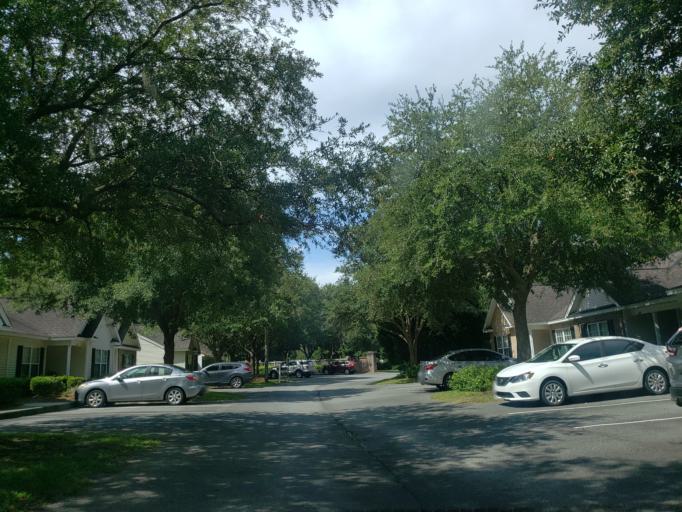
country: US
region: Georgia
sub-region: Chatham County
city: Wilmington Island
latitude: 32.0288
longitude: -80.9622
